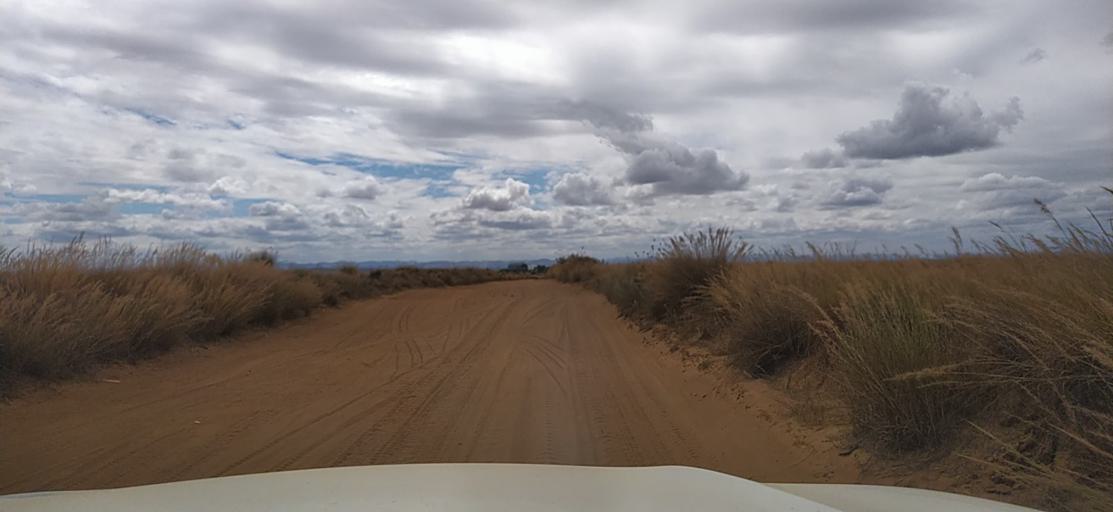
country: MG
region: Alaotra Mangoro
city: Ambatondrazaka
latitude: -17.9080
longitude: 48.2622
